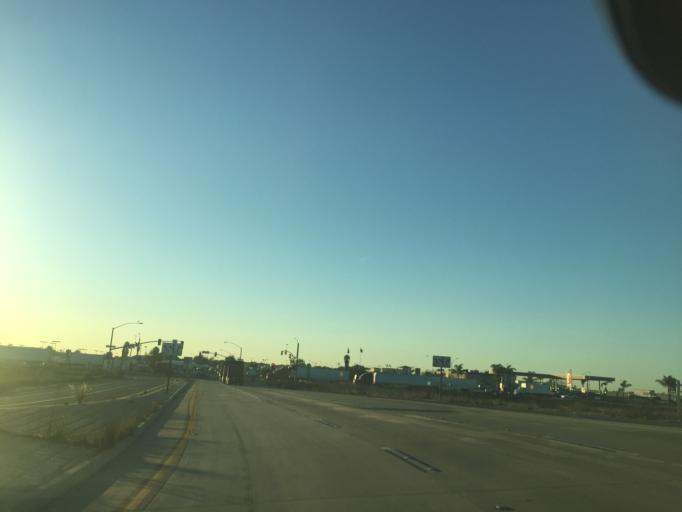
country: MX
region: Baja California
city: Tijuana
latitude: 32.5660
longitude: -116.9607
